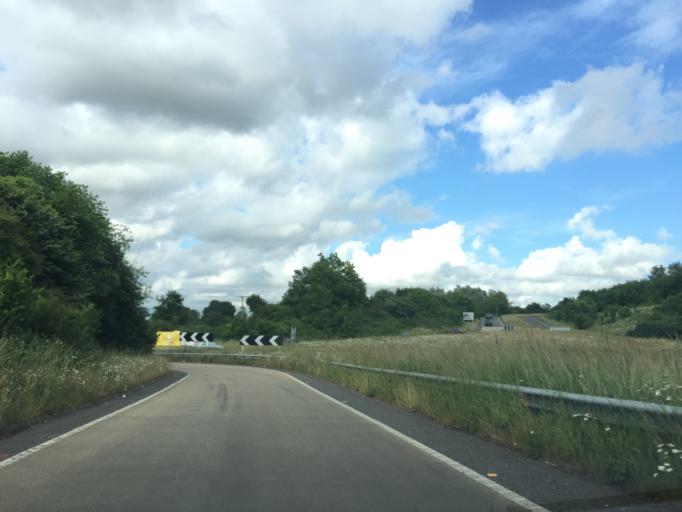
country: GB
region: England
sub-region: Hampshire
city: Totton
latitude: 50.9409
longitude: -1.5295
